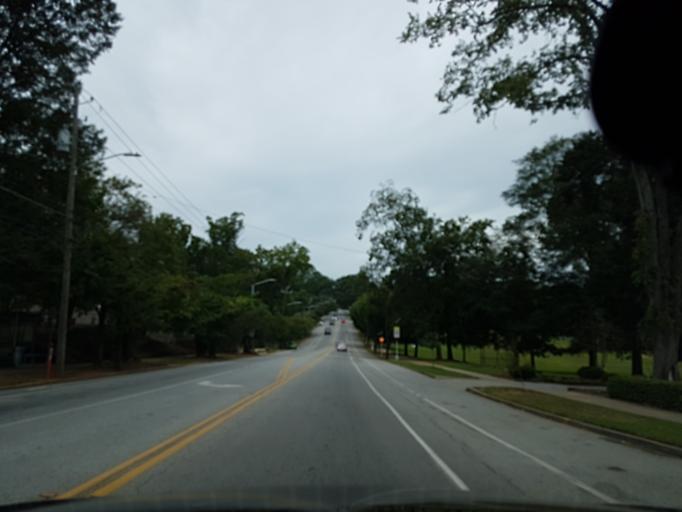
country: US
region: Georgia
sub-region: DeKalb County
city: Druid Hills
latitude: 33.7534
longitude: -84.3263
